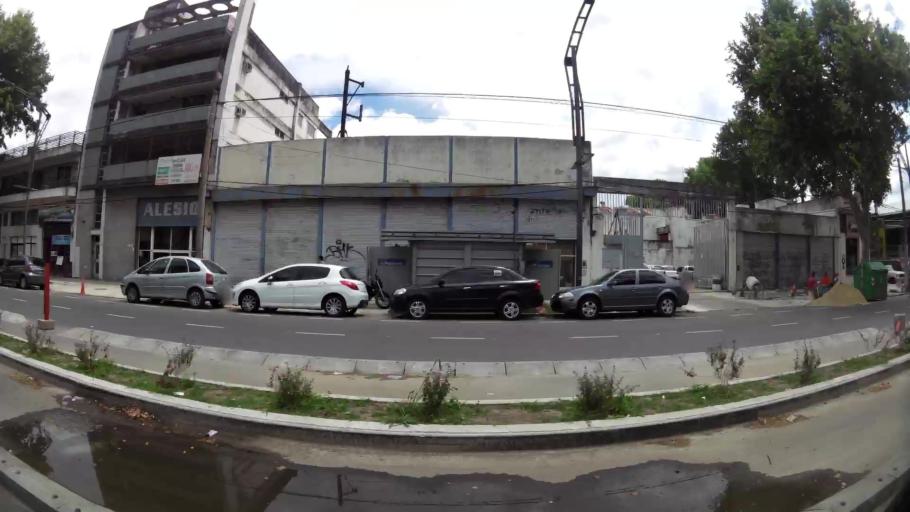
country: AR
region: Santa Fe
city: Gobernador Galvez
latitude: -32.9890
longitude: -60.6463
